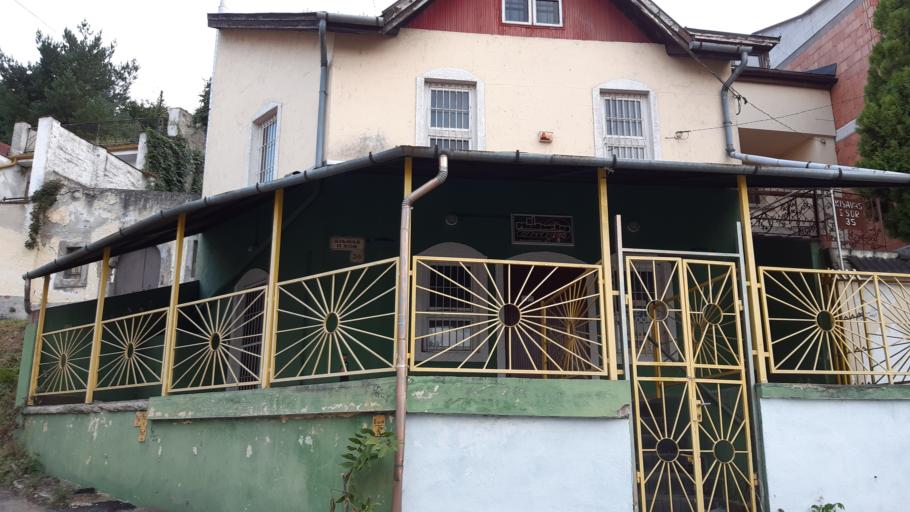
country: HU
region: Borsod-Abauj-Zemplen
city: Miskolc
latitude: 48.0986
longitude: 20.7836
